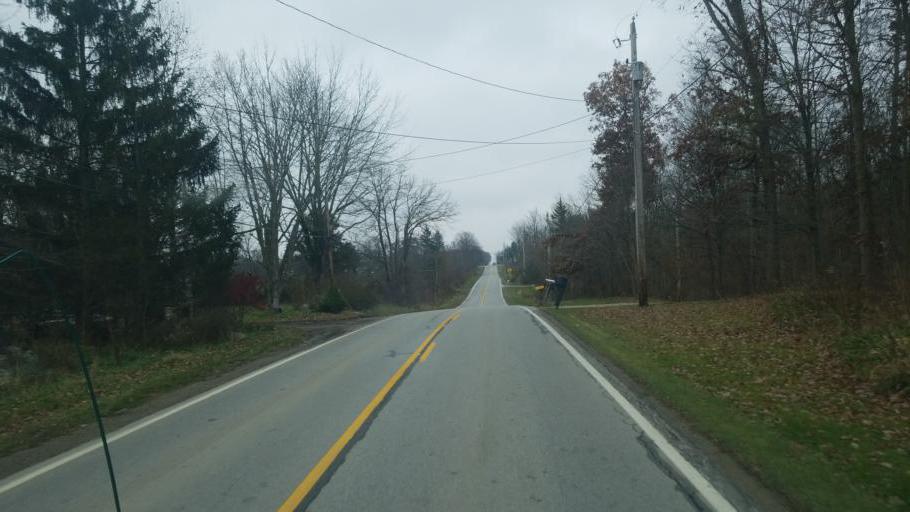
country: US
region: Ohio
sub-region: Medina County
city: Medina
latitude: 41.1359
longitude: -81.9289
